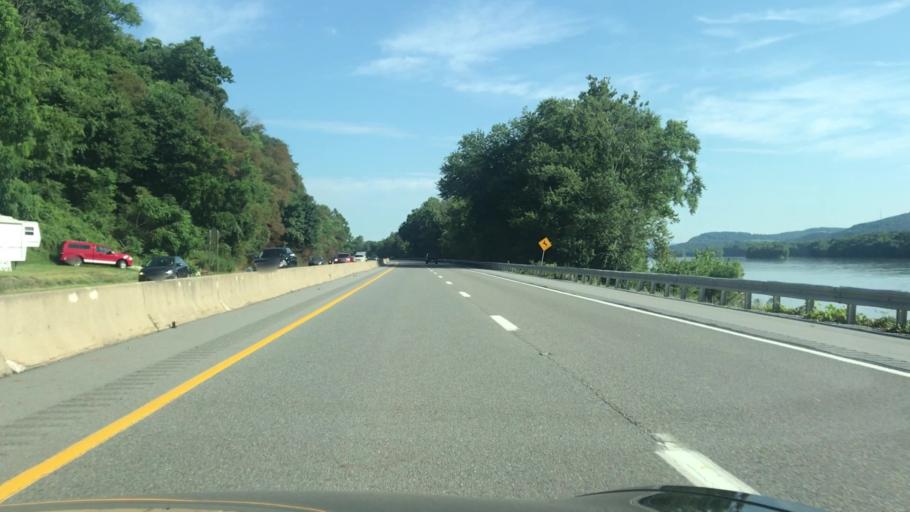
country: US
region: Pennsylvania
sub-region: Snyder County
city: Selinsgrove
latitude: 40.7421
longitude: -76.8568
